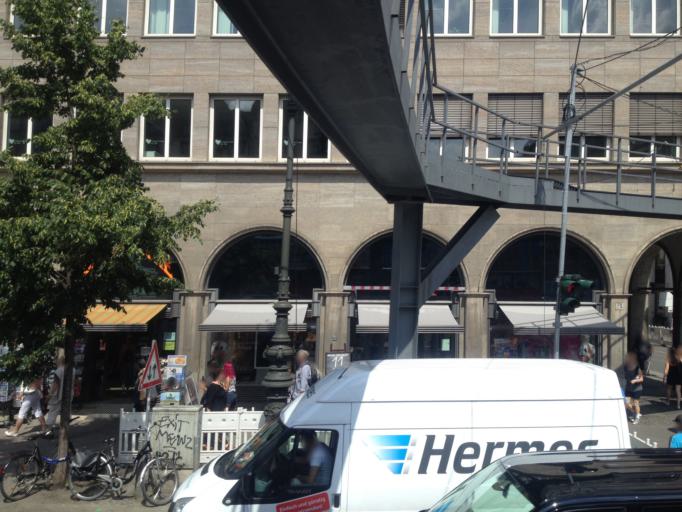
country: DE
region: Berlin
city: Mitte
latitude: 52.5172
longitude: 13.3884
